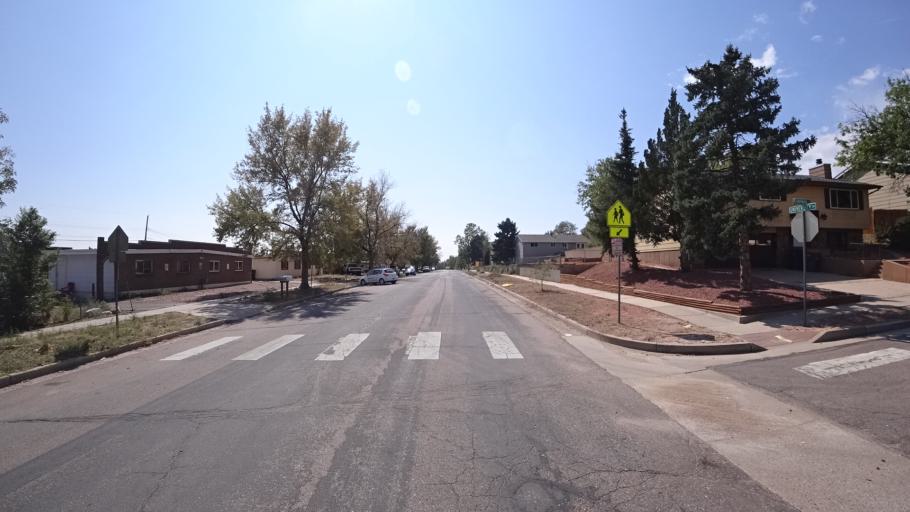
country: US
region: Colorado
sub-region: El Paso County
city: Colorado Springs
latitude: 38.8308
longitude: -104.7626
